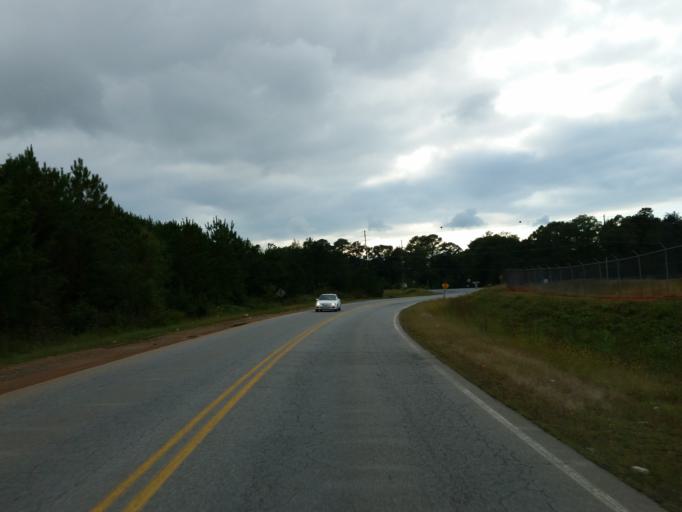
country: US
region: Georgia
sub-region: Bartow County
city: Cartersville
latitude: 34.1133
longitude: -84.8491
